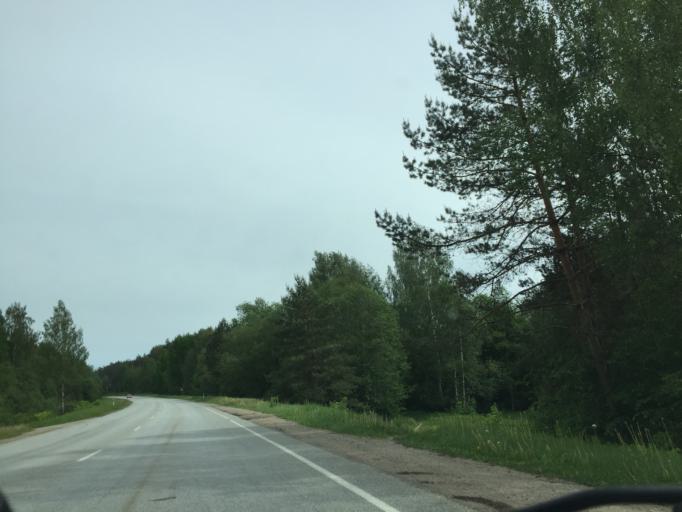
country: LV
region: Valmieras Rajons
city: Valmiera
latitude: 57.5128
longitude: 25.3916
